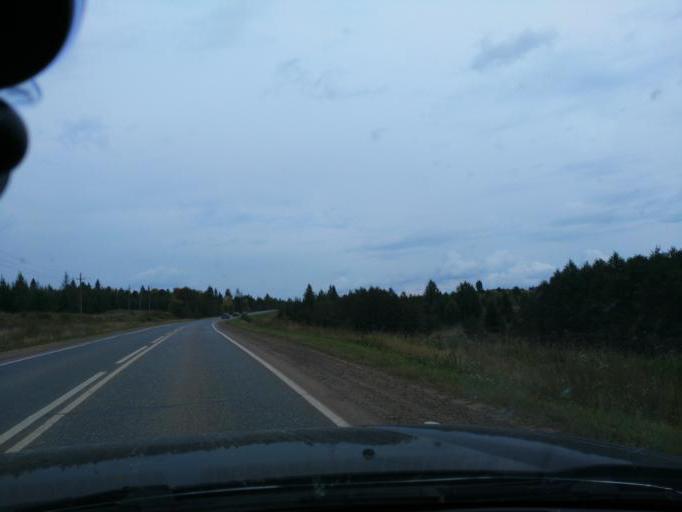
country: RU
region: Perm
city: Chernushka
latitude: 56.5070
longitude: 55.8772
